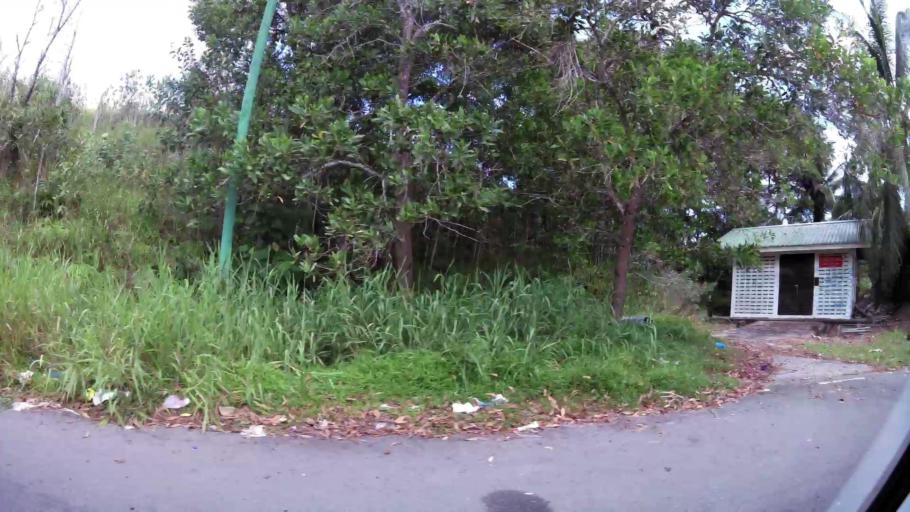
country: BN
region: Brunei and Muara
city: Bandar Seri Begawan
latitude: 4.9306
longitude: 114.8935
